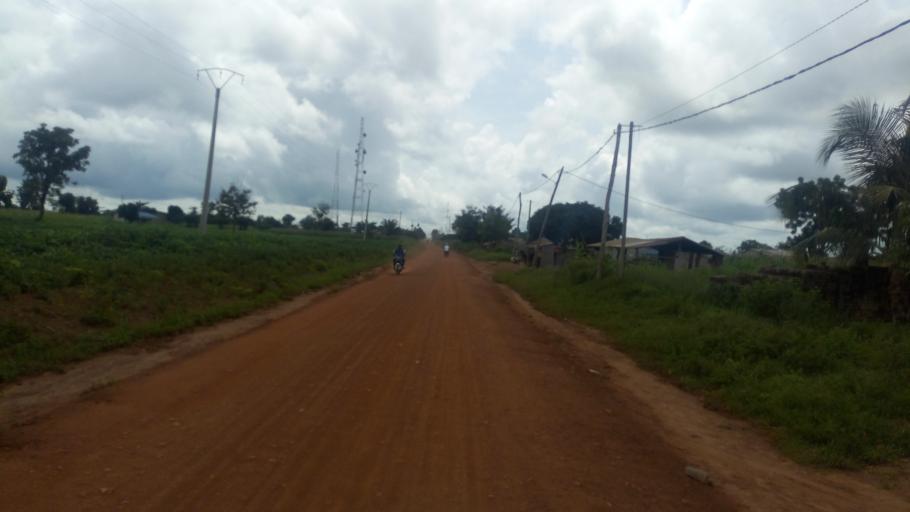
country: TG
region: Centrale
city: Sotouboua
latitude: 8.5563
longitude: 0.9997
